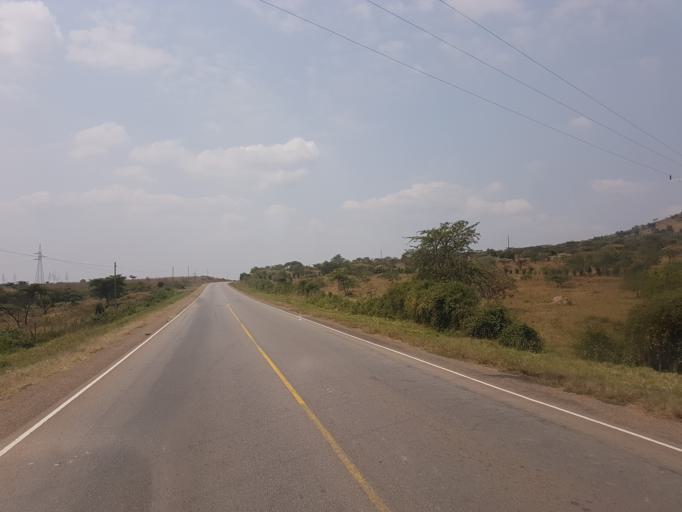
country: UG
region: Western Region
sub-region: Mbarara District
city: Mbarara
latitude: -0.4883
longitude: 30.8580
